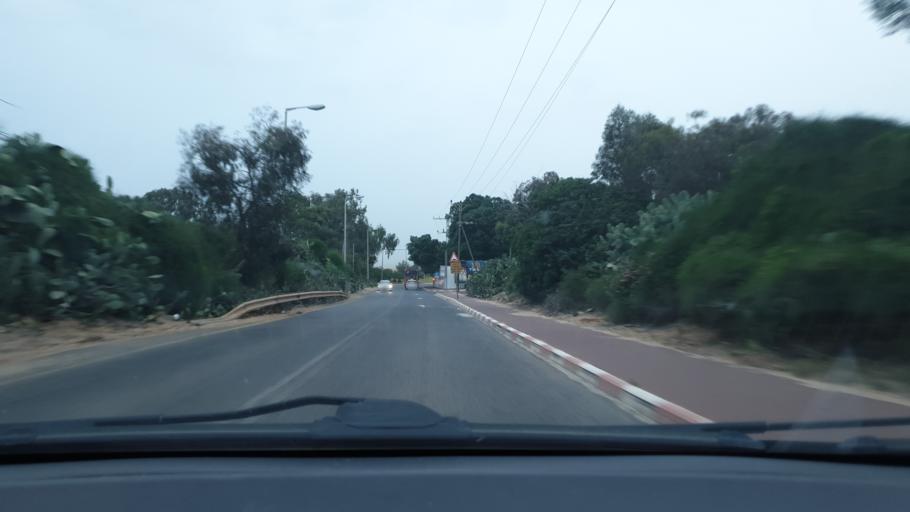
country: IL
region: Central District
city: Kefar Habad
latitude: 31.9853
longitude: 34.8428
